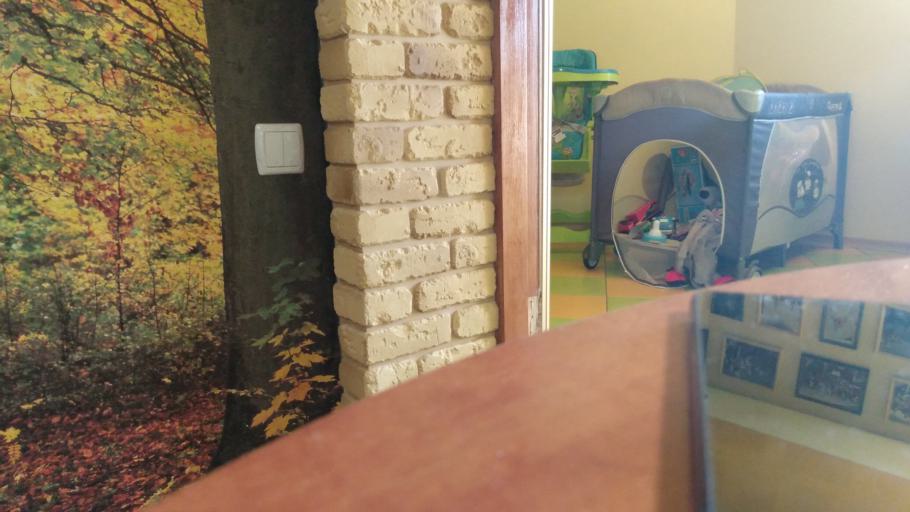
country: RU
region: Tverskaya
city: Bologoye
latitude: 57.9299
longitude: 34.2021
